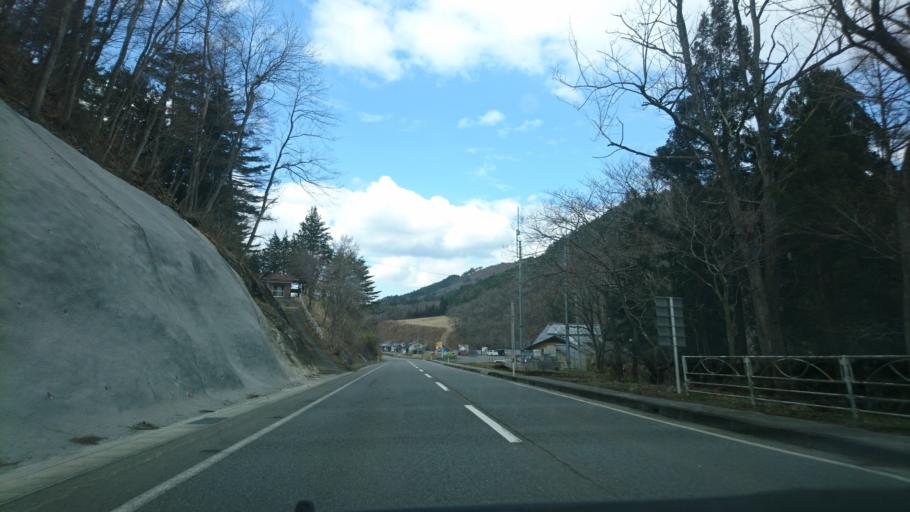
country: JP
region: Iwate
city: Tono
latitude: 39.2695
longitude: 141.4207
